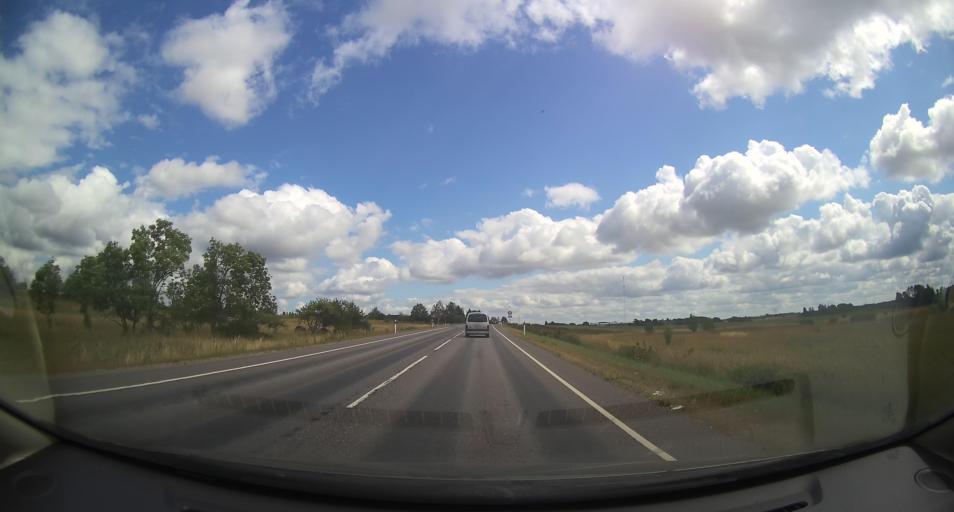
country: EE
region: Laeaene
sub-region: Lihula vald
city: Lihula
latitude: 58.7245
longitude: 23.9231
